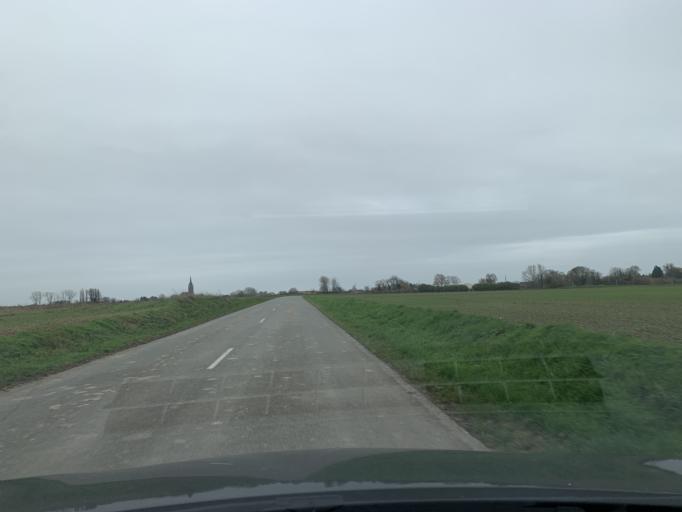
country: FR
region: Nord-Pas-de-Calais
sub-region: Departement du Nord
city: Aubigny-au-Bac
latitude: 50.2354
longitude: 3.1553
